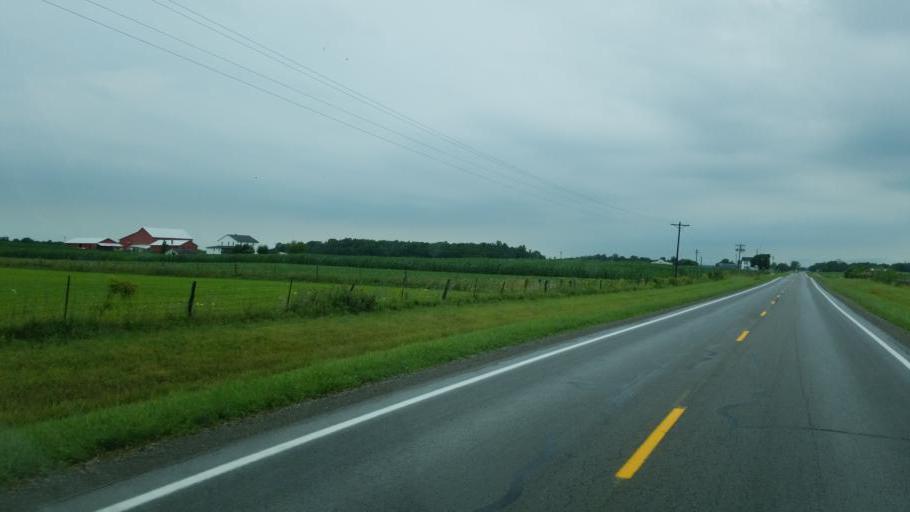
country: US
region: Ohio
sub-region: Hardin County
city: Kenton
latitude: 40.5747
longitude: -83.5906
